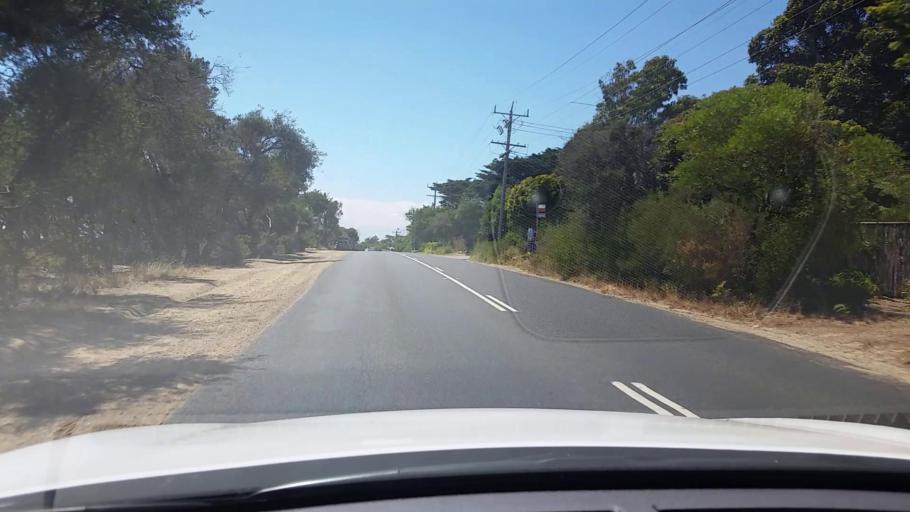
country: AU
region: Victoria
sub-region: Mornington Peninsula
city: Mount Martha
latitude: -38.2590
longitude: 145.0220
